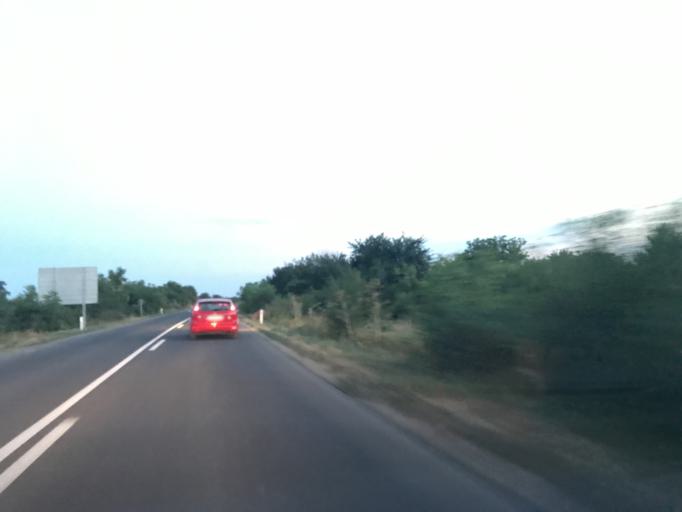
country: RS
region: Central Serbia
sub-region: Branicevski Okrug
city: Pozarevac
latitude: 44.6194
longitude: 21.1461
